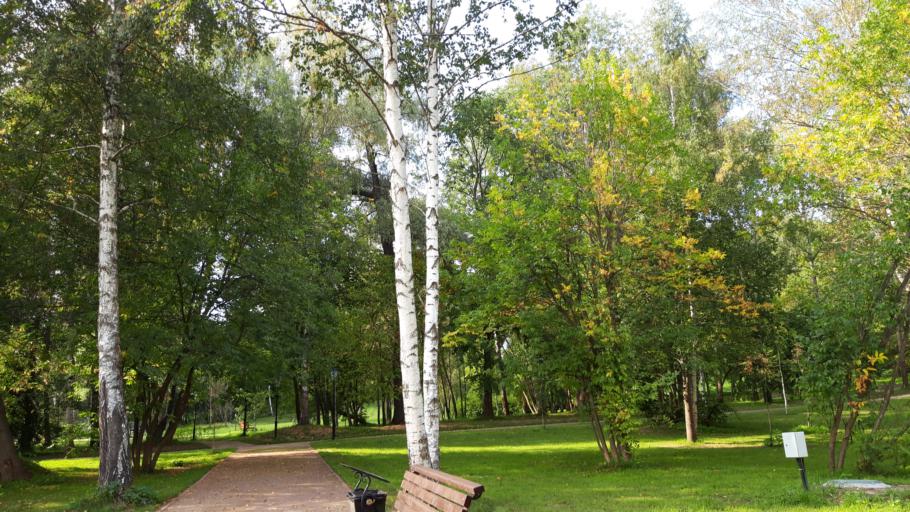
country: RU
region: Moskovskaya
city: Mendeleyevo
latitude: 56.0477
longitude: 37.2225
